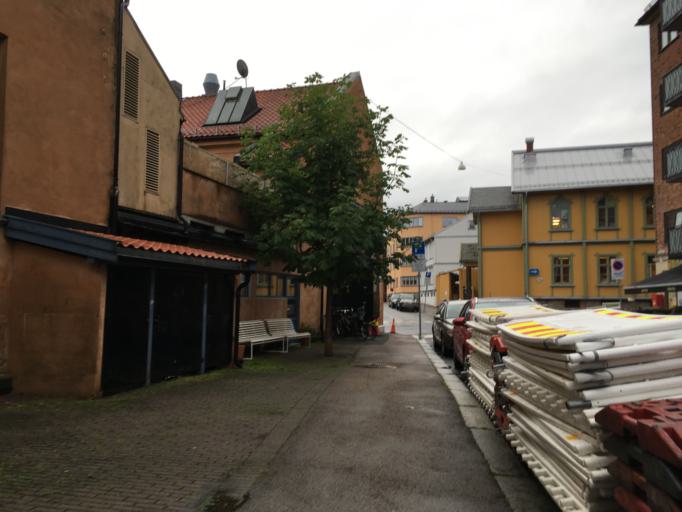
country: NO
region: Oslo
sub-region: Oslo
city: Oslo
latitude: 59.9139
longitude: 10.7816
